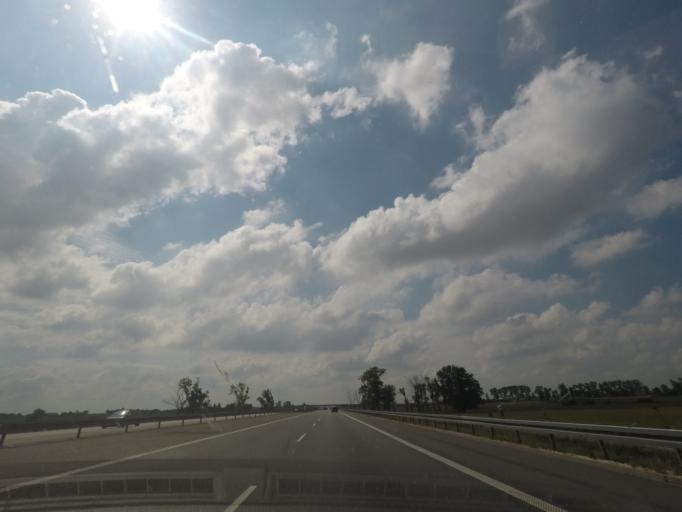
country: PL
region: Lodz Voivodeship
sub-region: Powiat kutnowski
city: Krzyzanow
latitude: 52.1760
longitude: 19.4858
